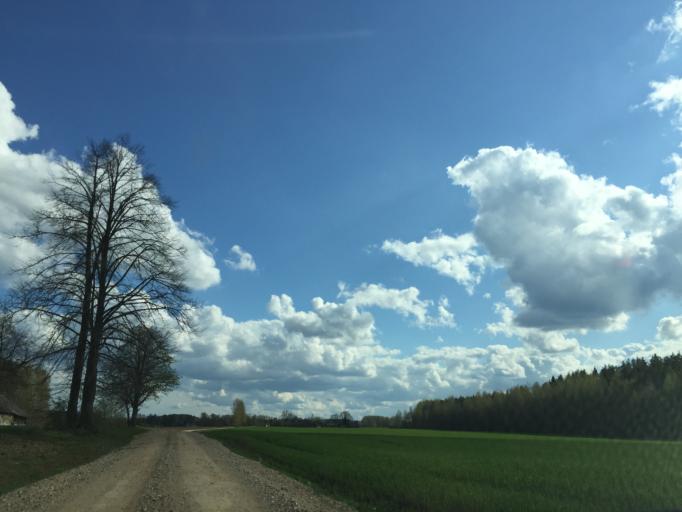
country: LV
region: Beverina
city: Murmuiza
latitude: 57.4276
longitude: 25.5494
